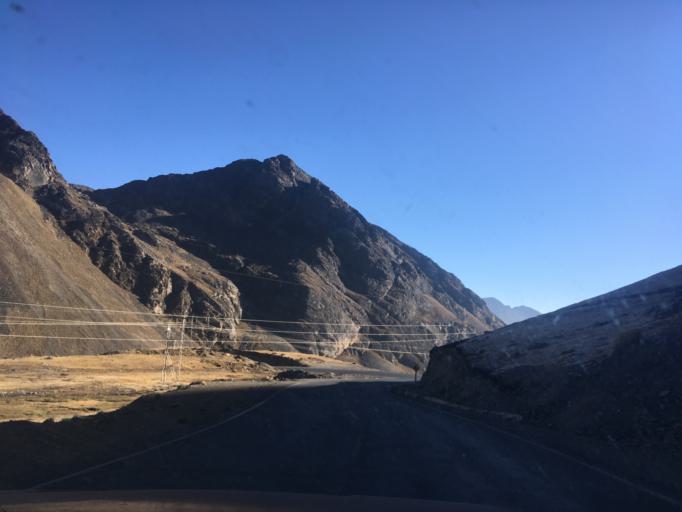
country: BO
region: La Paz
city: Quime
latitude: -17.0446
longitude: -67.2911
